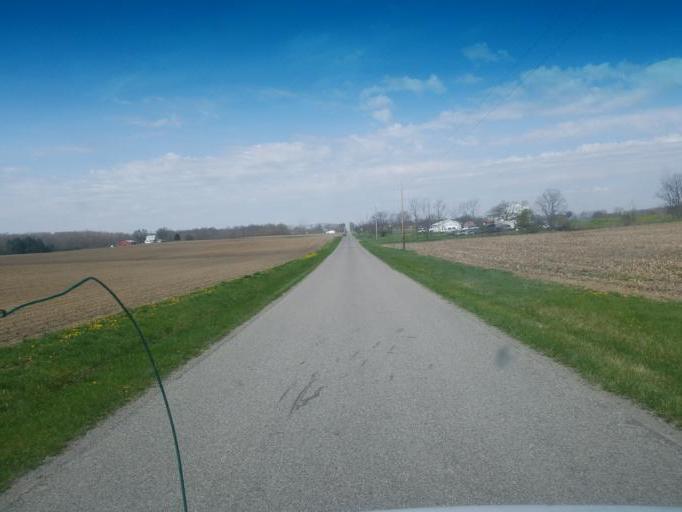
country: US
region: Ohio
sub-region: Logan County
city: Northwood
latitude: 40.4982
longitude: -83.6599
